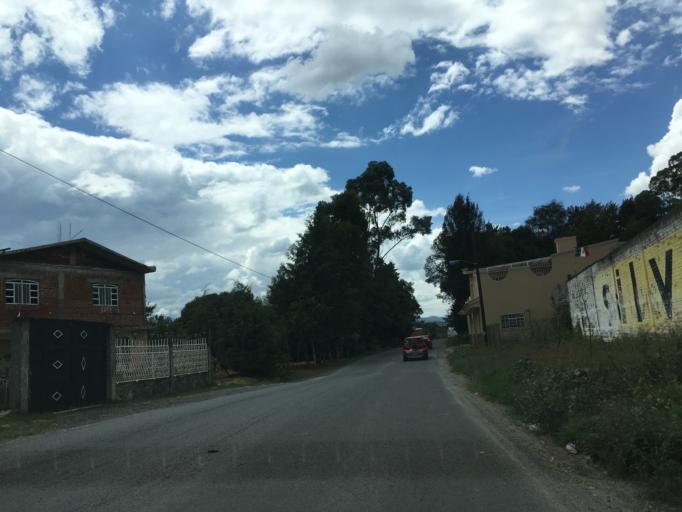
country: MX
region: Michoacan
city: Zacapu
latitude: 19.8376
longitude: -101.7608
